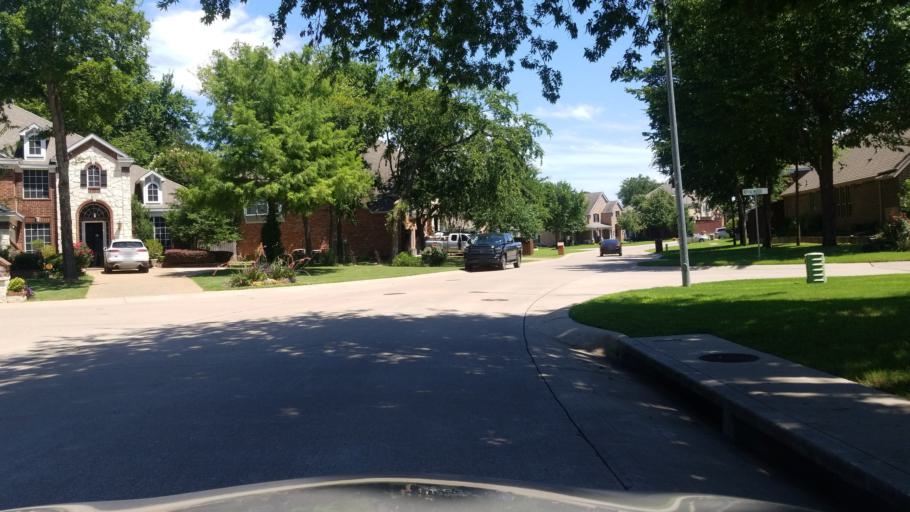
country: US
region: Texas
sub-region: Dallas County
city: Grand Prairie
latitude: 32.6828
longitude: -96.9998
